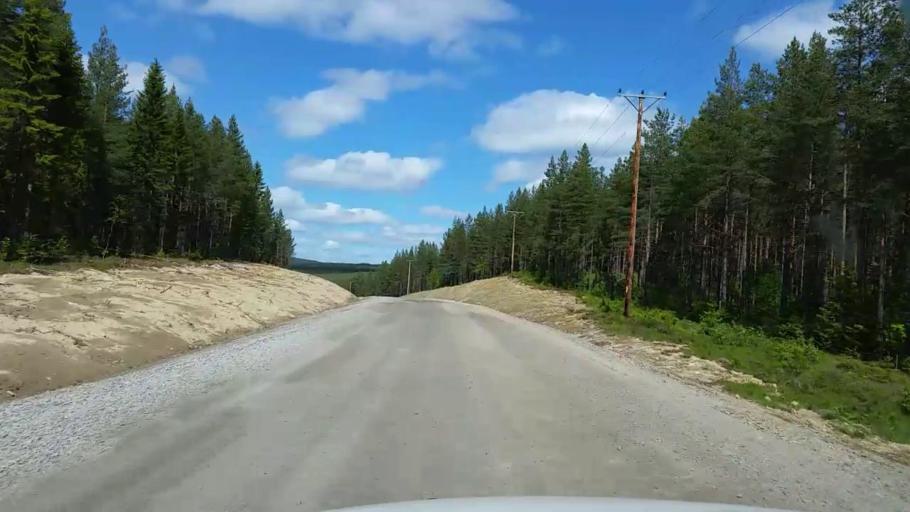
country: SE
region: Gaevleborg
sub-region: Ljusdals Kommun
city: Farila
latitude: 61.5876
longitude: 15.9167
